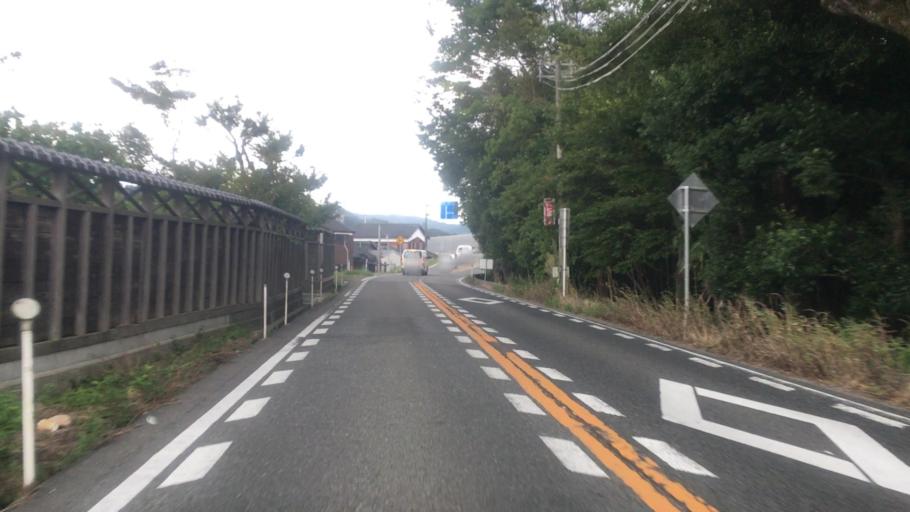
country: JP
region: Hyogo
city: Toyooka
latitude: 35.4757
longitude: 134.7867
